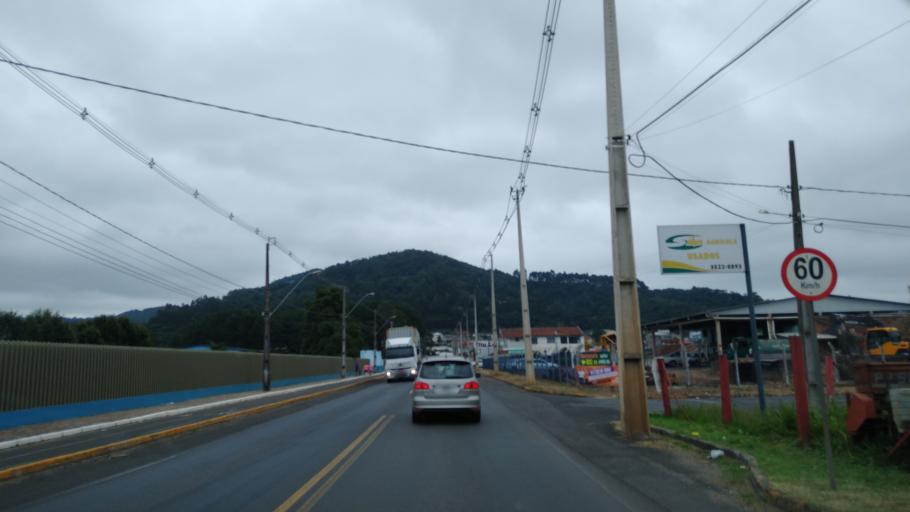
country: BR
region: Santa Catarina
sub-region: Porto Uniao
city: Porto Uniao
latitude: -26.2566
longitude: -51.0686
